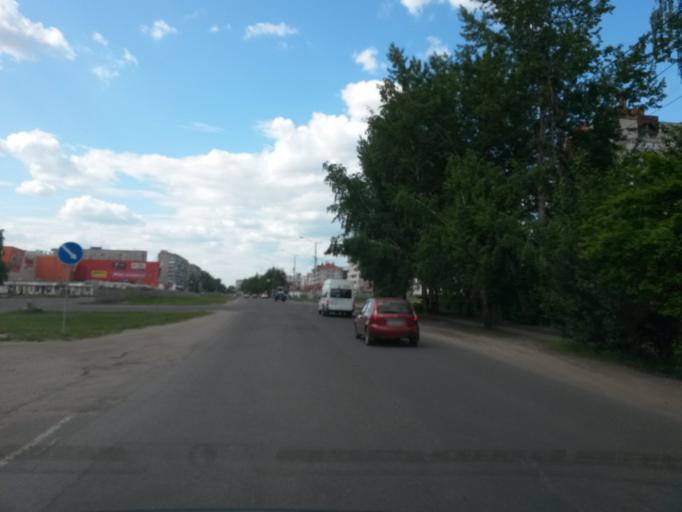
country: RU
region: Jaroslavl
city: Yaroslavl
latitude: 57.6439
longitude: 39.9570
